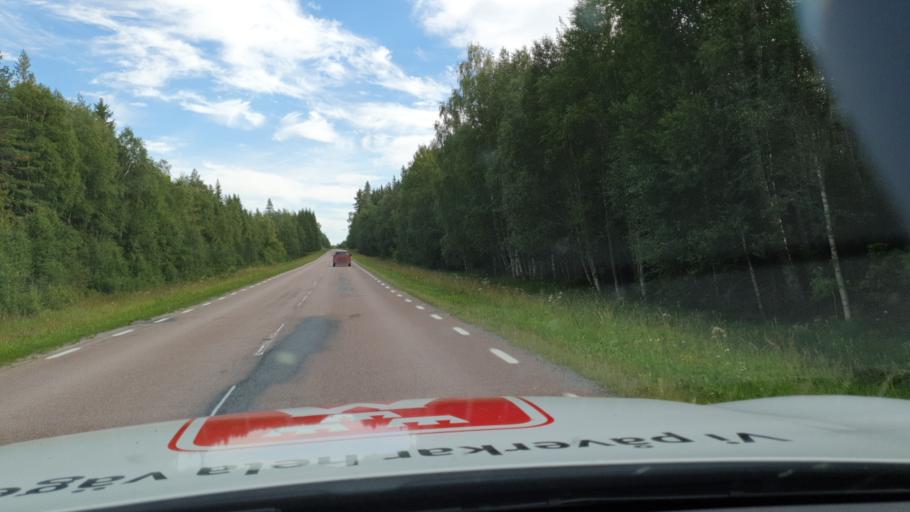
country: SE
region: Jaemtland
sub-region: Stroemsunds Kommun
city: Stroemsund
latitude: 63.7019
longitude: 15.8828
